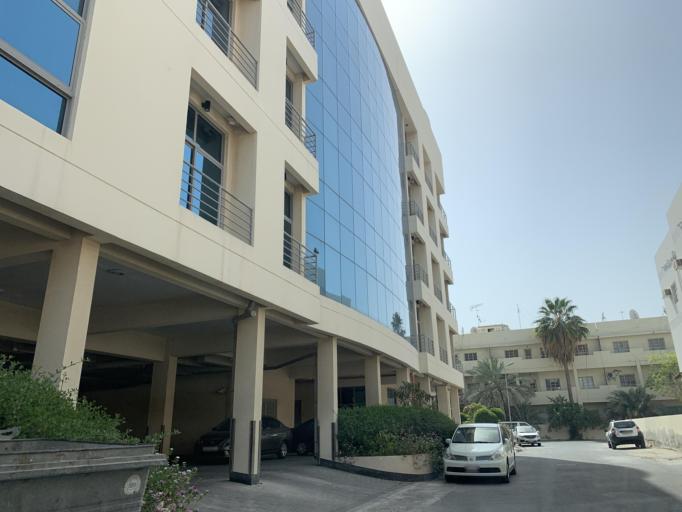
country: BH
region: Manama
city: Manama
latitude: 26.2098
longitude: 50.5870
